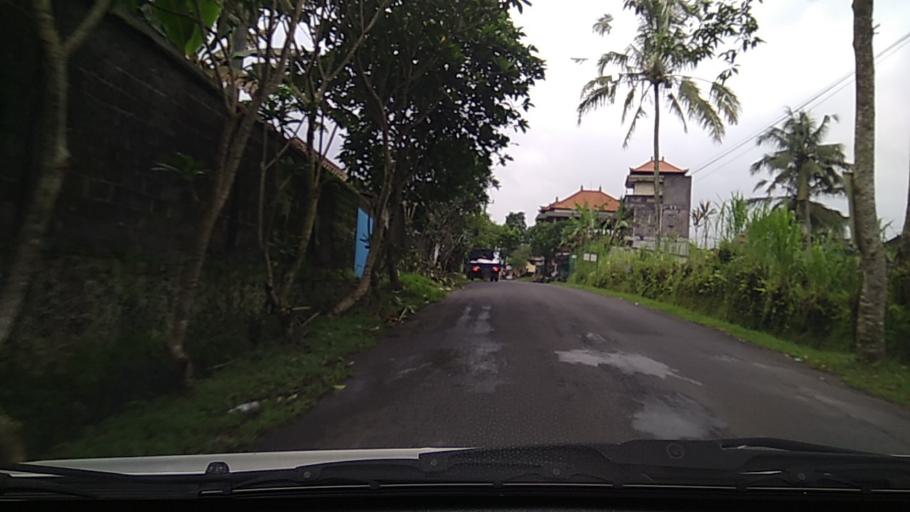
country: ID
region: Bali
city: Banjar Manukayaanyar
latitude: -8.4185
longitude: 115.3000
